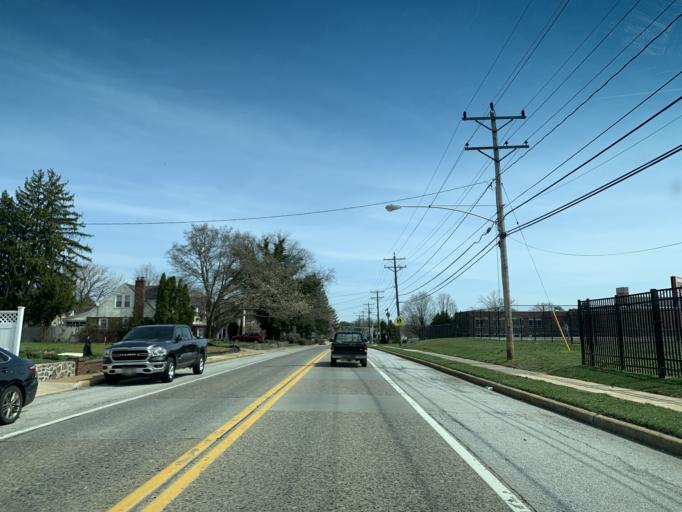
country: US
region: Delaware
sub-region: New Castle County
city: Newport
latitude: 39.7242
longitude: -75.6028
